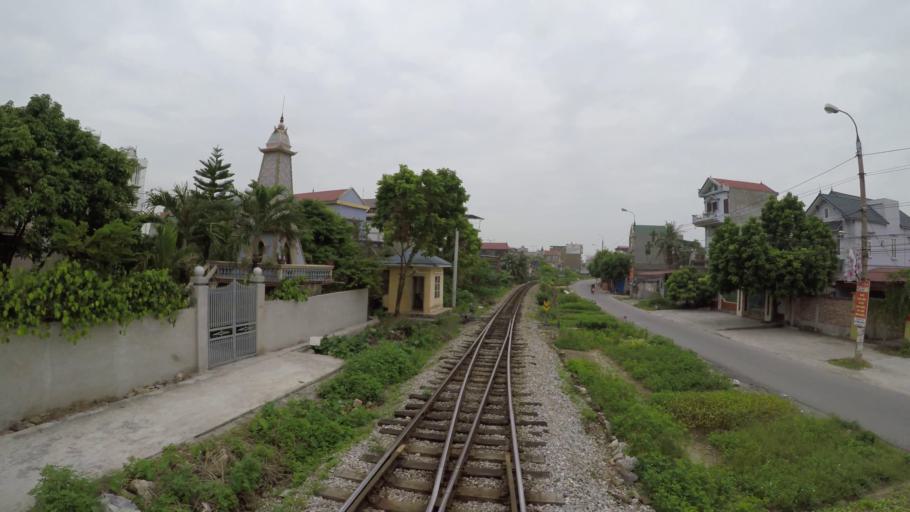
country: VN
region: Hai Duong
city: Phu Thai
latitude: 20.9683
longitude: 106.5024
